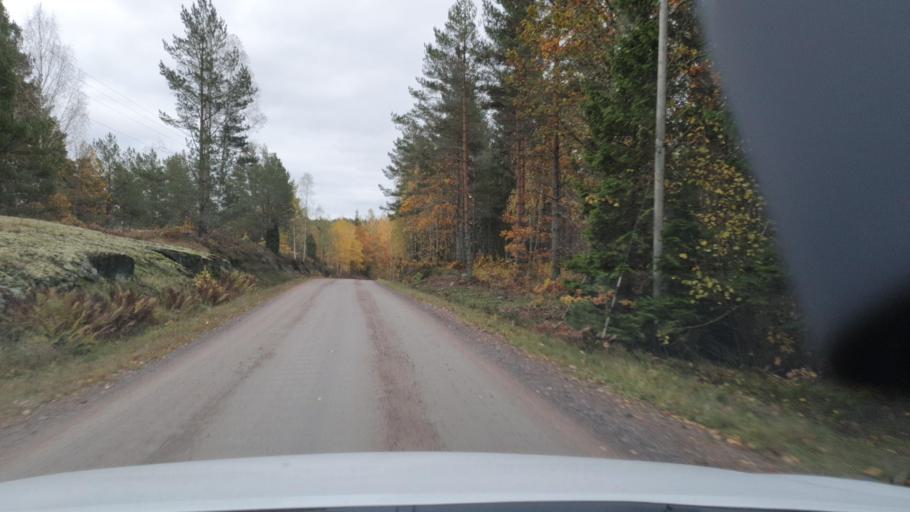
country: SE
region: Kalmar
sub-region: Vasterviks Kommun
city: Ankarsrum
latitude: 57.6965
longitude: 16.4626
